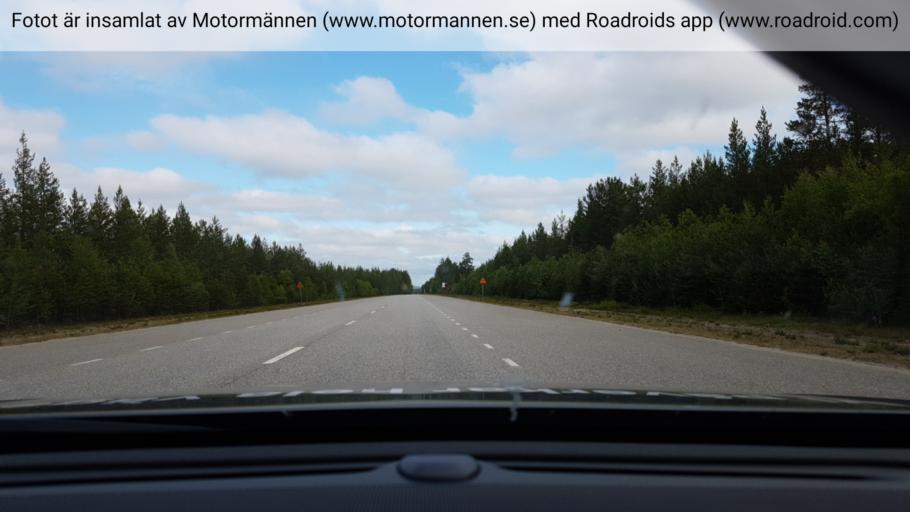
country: SE
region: Vaesterbotten
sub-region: Norsjo Kommun
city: Norsjoe
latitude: 64.5732
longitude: 19.3086
